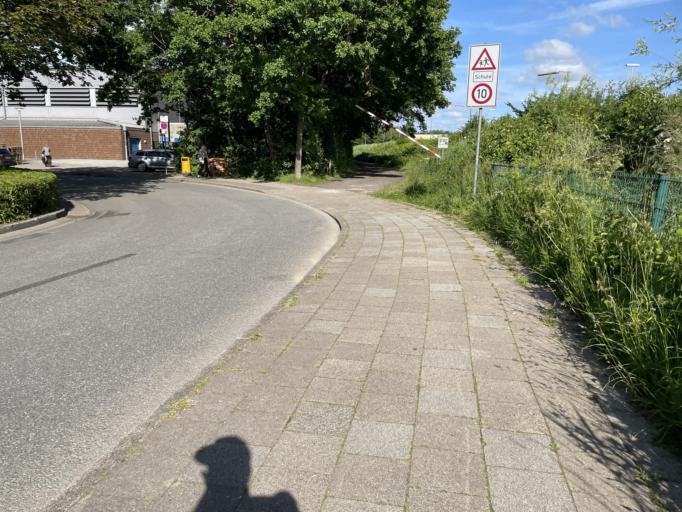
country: DE
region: Schleswig-Holstein
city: Husum
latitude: 54.4722
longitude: 9.0587
